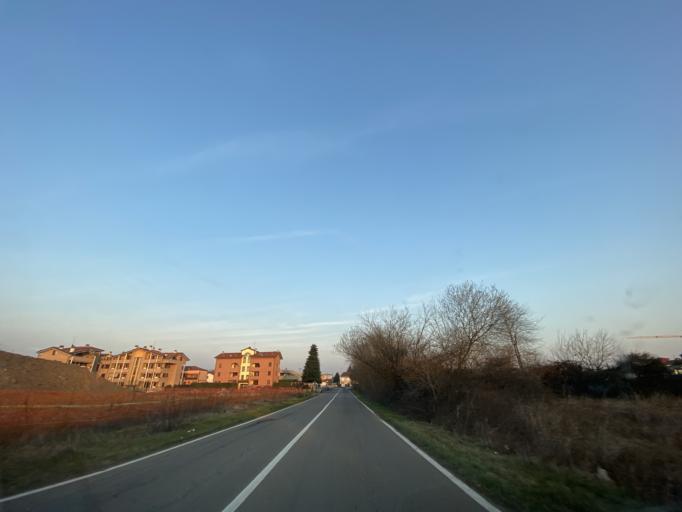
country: IT
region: Lombardy
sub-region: Citta metropolitana di Milano
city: Cesate
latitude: 45.6020
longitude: 9.0759
